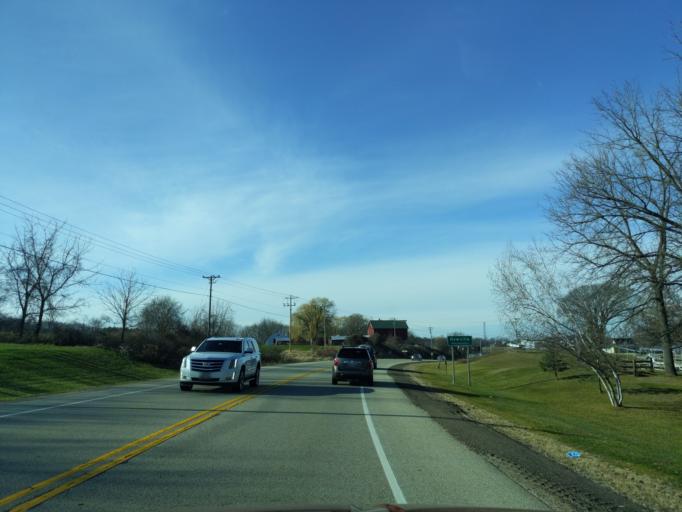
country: US
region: Wisconsin
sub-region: Rock County
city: Edgerton
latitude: 42.8272
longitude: -89.0176
